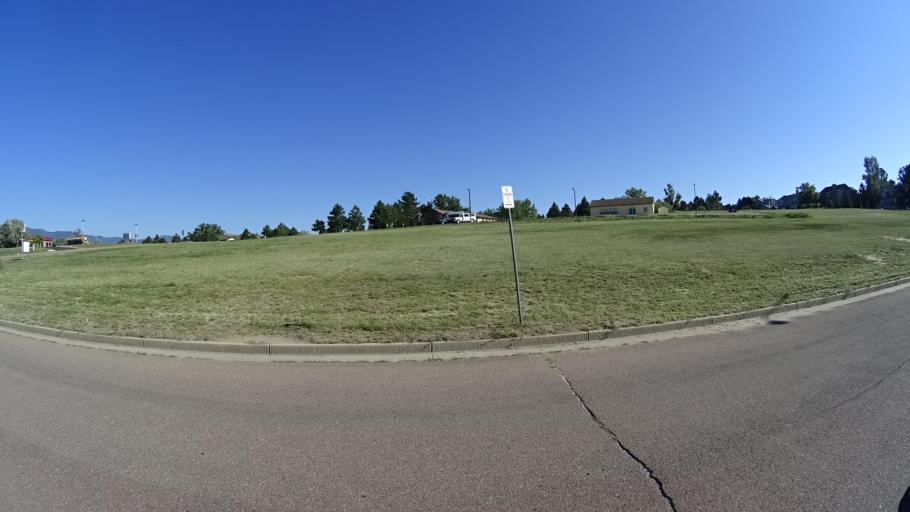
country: US
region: Colorado
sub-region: El Paso County
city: Air Force Academy
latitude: 38.9691
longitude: -104.7952
